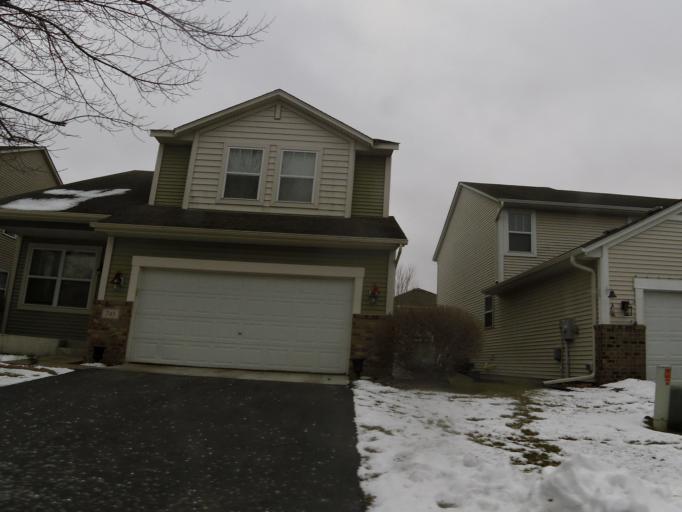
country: US
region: Minnesota
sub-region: Carver County
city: Chaska
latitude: 44.8068
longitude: -93.6184
